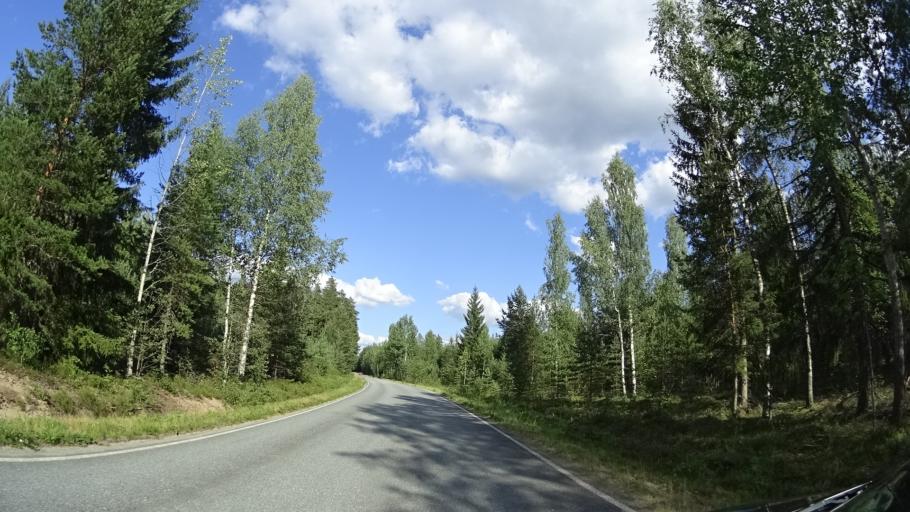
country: FI
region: Uusimaa
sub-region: Helsinki
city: Kaerkoelae
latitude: 60.7393
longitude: 24.0935
